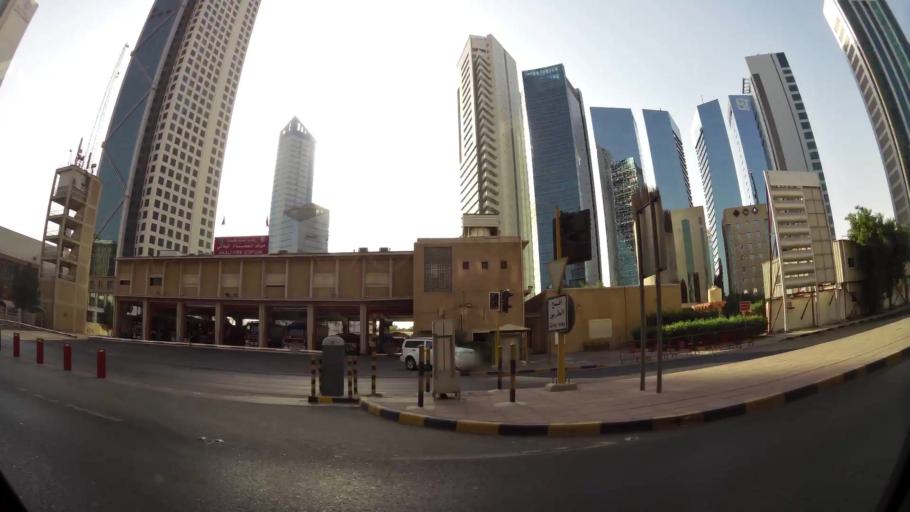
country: KW
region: Al Asimah
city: Kuwait City
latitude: 29.3768
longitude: 47.9885
